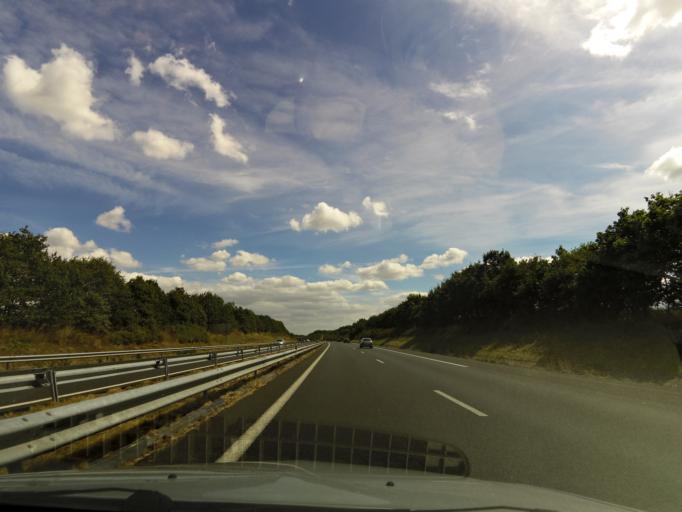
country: FR
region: Pays de la Loire
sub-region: Departement de la Vendee
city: Chauche
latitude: 46.8525
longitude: -1.2758
